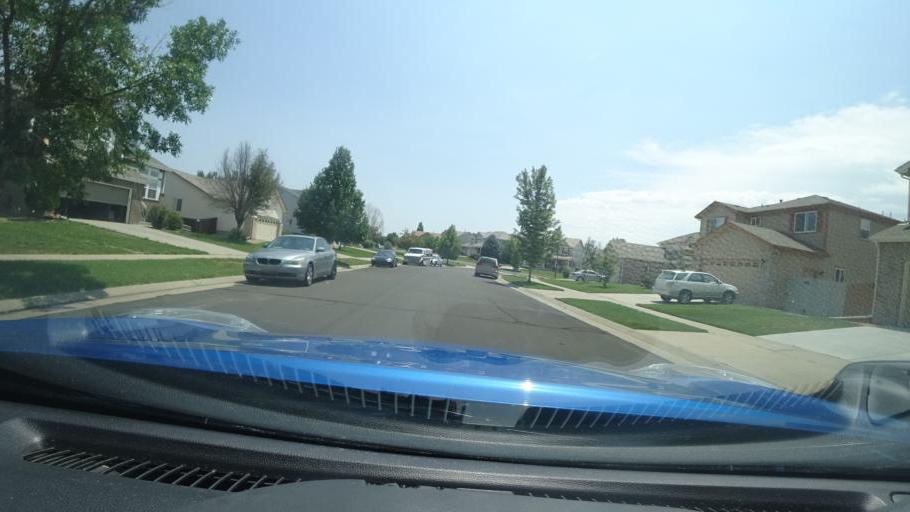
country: US
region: Colorado
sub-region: Adams County
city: Aurora
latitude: 39.6739
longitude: -104.7657
